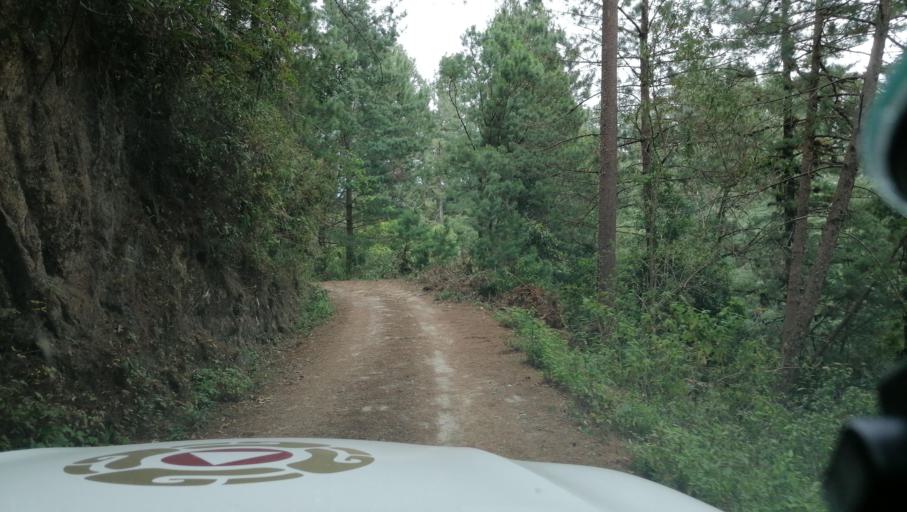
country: MX
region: Chiapas
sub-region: Tapachula
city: Canton Villaflor
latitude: 15.2002
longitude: -92.2334
